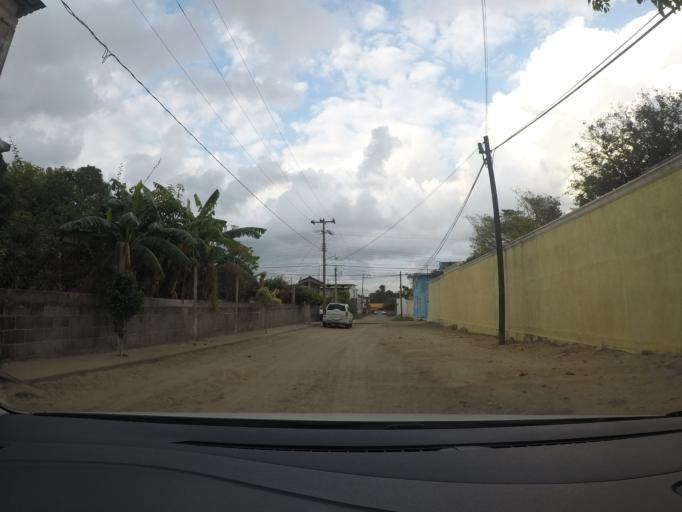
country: MX
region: Oaxaca
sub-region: Salina Cruz
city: Salina Cruz
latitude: 16.2066
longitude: -95.1983
